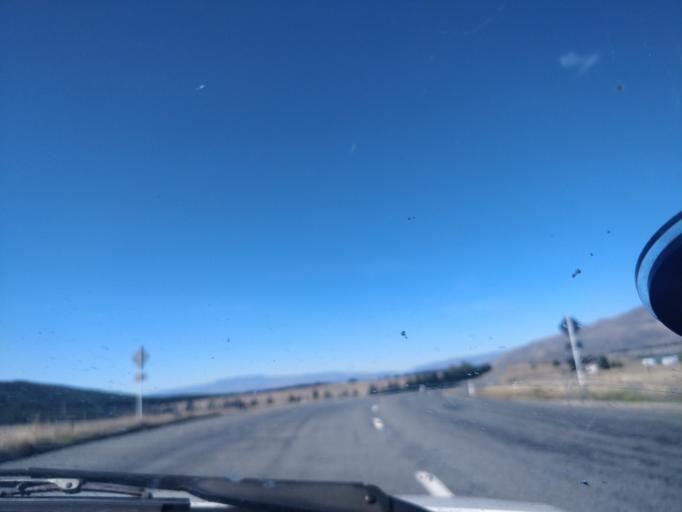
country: NZ
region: Otago
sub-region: Queenstown-Lakes District
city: Wanaka
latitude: -44.2663
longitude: 170.0362
